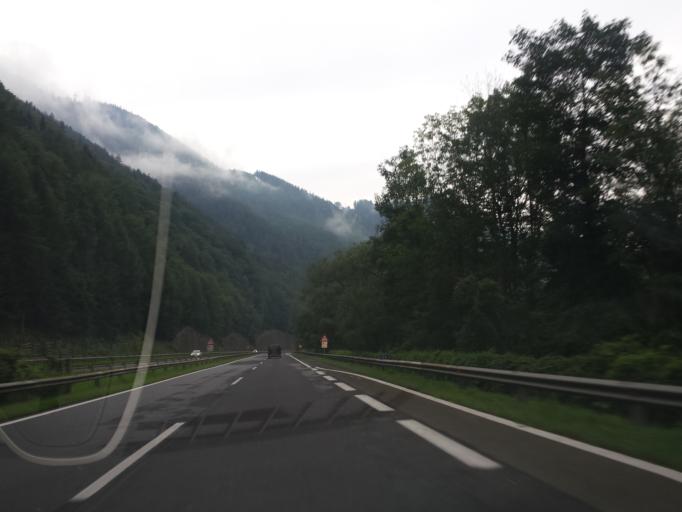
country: AT
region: Styria
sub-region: Politischer Bezirk Bruck-Muerzzuschlag
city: Bruck an der Mur
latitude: 47.3908
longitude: 15.2967
